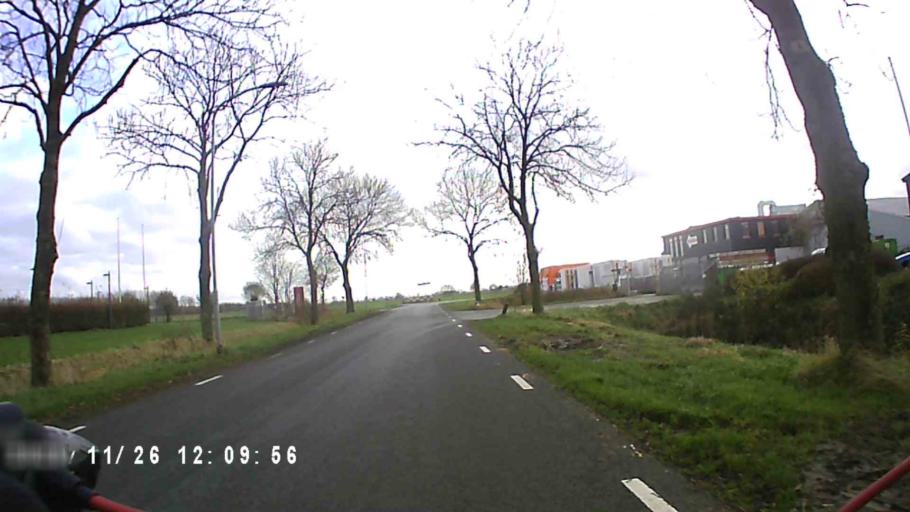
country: NL
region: Groningen
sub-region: Gemeente Bedum
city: Bedum
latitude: 53.3370
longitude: 6.6357
